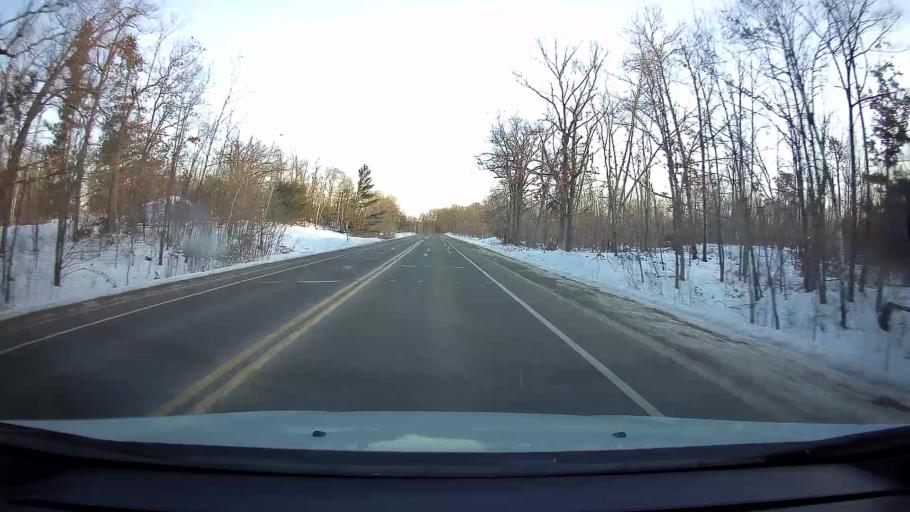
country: US
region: Wisconsin
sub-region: Barron County
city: Turtle Lake
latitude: 45.4120
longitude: -92.1352
